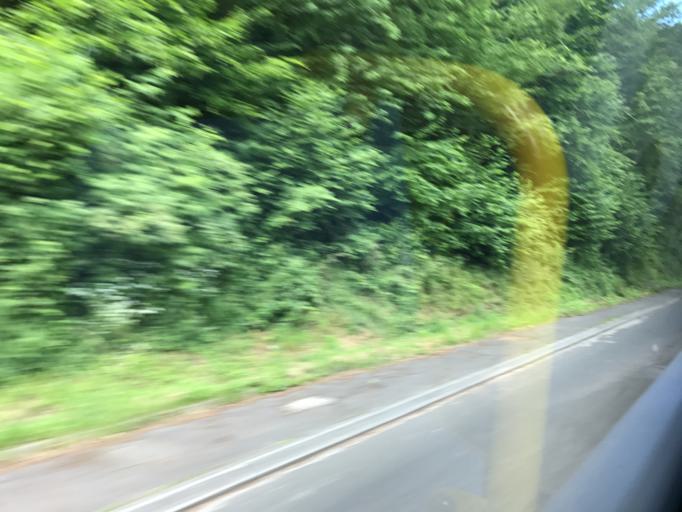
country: DE
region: Hesse
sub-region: Regierungsbezirk Darmstadt
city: Schlangenbad
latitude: 50.0664
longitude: 8.1091
